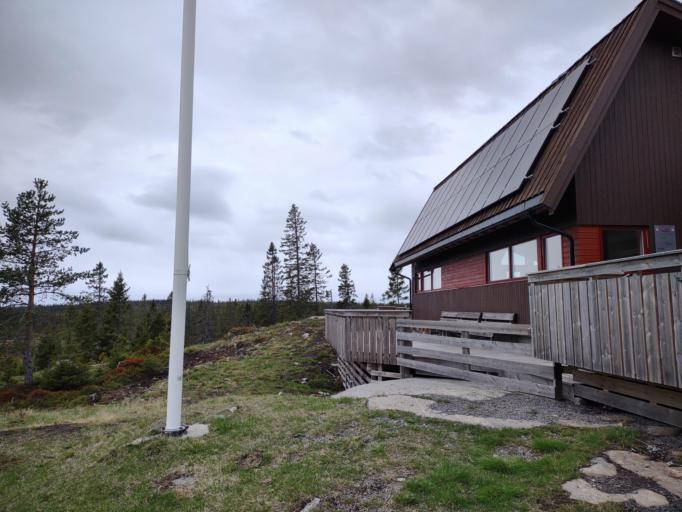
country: NO
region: Oppland
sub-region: Gran
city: Jaren
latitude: 60.4314
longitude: 10.6809
